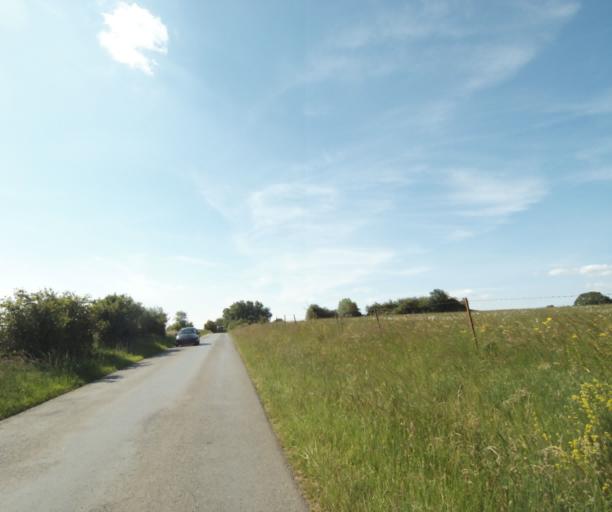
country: FR
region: Champagne-Ardenne
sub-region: Departement des Ardennes
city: Warcq
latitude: 49.7899
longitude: 4.6908
